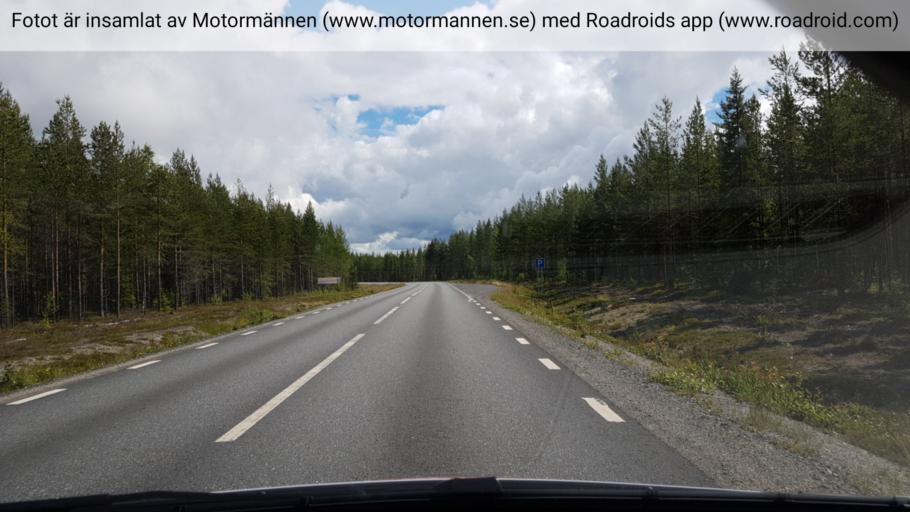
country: SE
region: Vaesterbotten
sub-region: Bjurholms Kommun
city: Bjurholm
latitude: 64.2931
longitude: 19.1851
